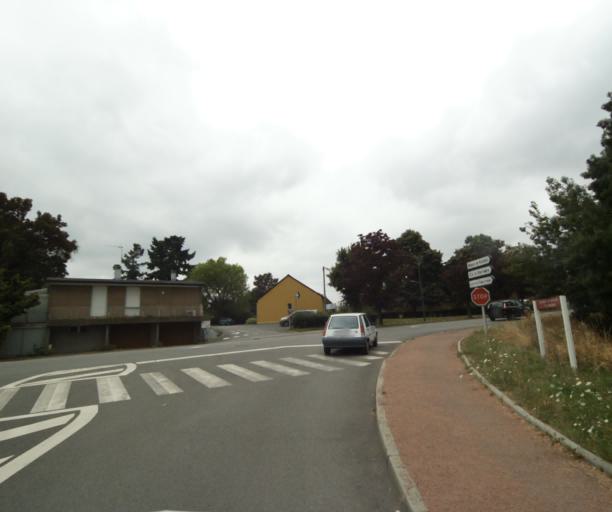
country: FR
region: Pays de la Loire
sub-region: Departement de la Sarthe
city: Sable-sur-Sarthe
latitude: 47.8392
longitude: -0.3139
